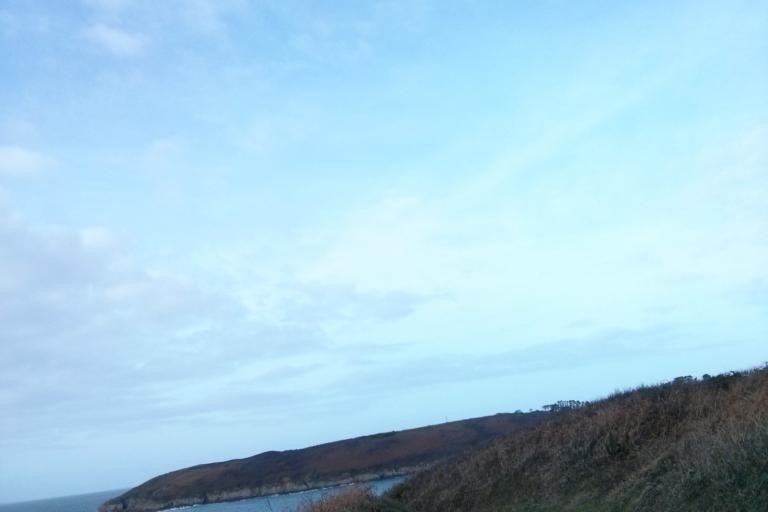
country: FR
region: Brittany
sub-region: Departement du Finistere
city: Le Conquet
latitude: 48.4010
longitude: -4.7744
